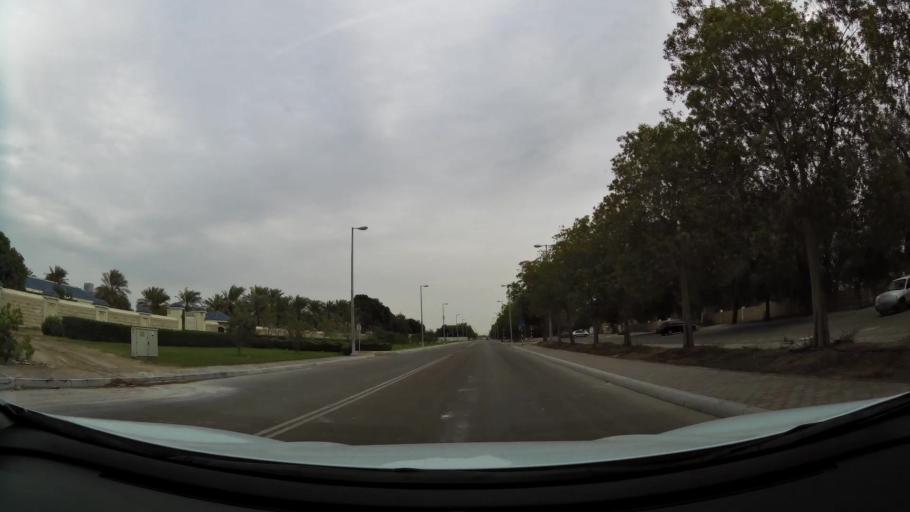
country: AE
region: Abu Dhabi
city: Abu Dhabi
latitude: 24.4123
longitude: 54.4303
